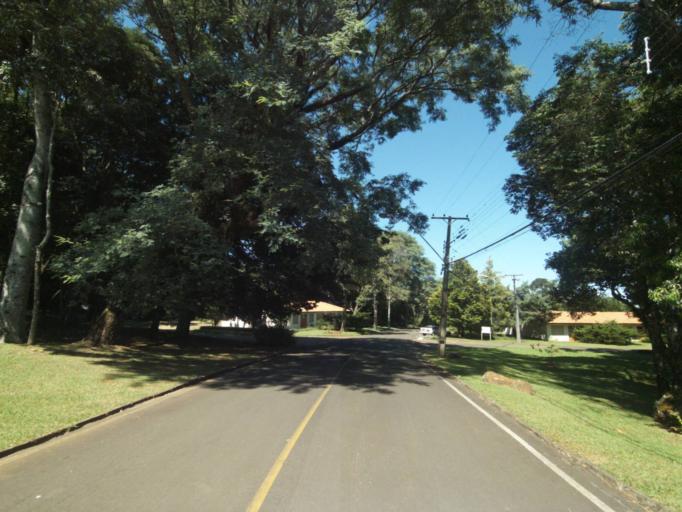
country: BR
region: Parana
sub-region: Chopinzinho
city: Chopinzinho
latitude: -25.7990
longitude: -52.0992
